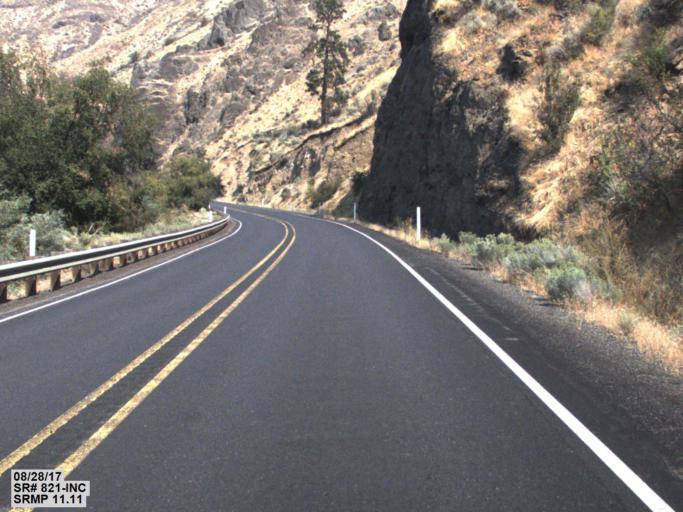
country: US
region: Washington
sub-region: Yakima County
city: Selah
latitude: 46.8009
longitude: -120.4454
